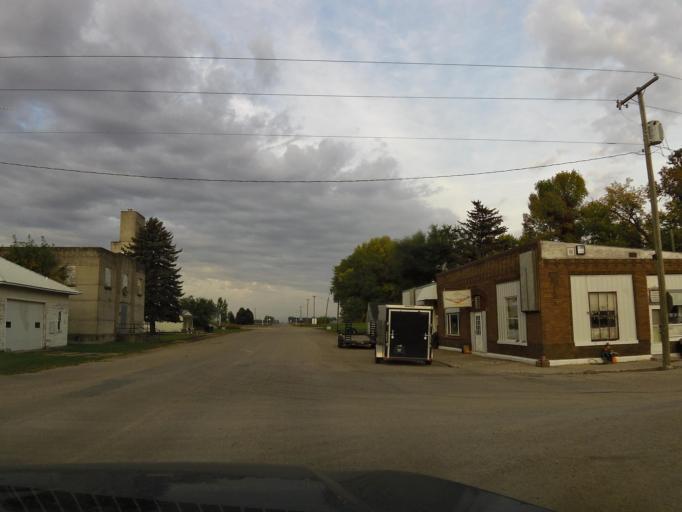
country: US
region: North Dakota
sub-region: Pembina County
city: Cavalier
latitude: 48.6882
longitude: -97.6663
